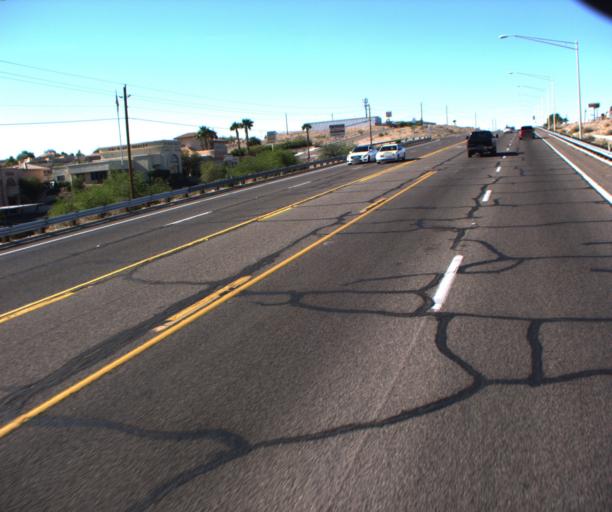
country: US
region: Arizona
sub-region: Mohave County
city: Bullhead City
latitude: 35.0459
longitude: -114.5897
